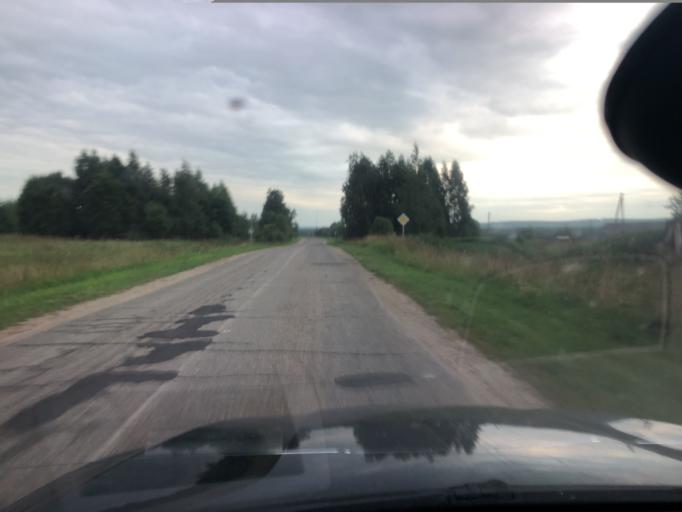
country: RU
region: Jaroslavl
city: Pereslavl'-Zalesskiy
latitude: 57.0106
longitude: 38.9732
